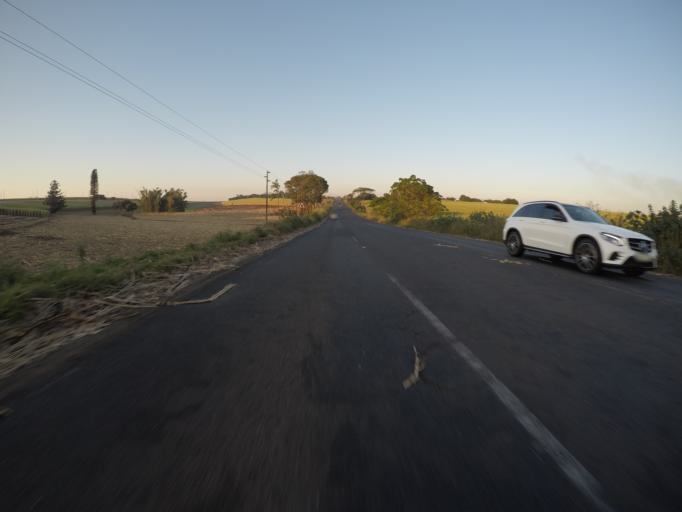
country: ZA
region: KwaZulu-Natal
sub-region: uThungulu District Municipality
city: Empangeni
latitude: -28.7865
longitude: 31.8974
